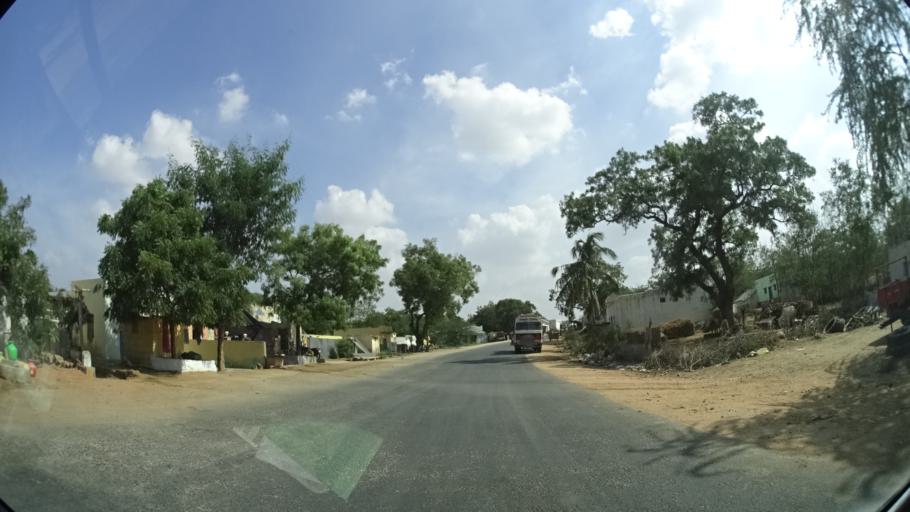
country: IN
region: Andhra Pradesh
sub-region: Anantapur
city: Uravakonda
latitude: 14.8254
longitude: 77.3420
